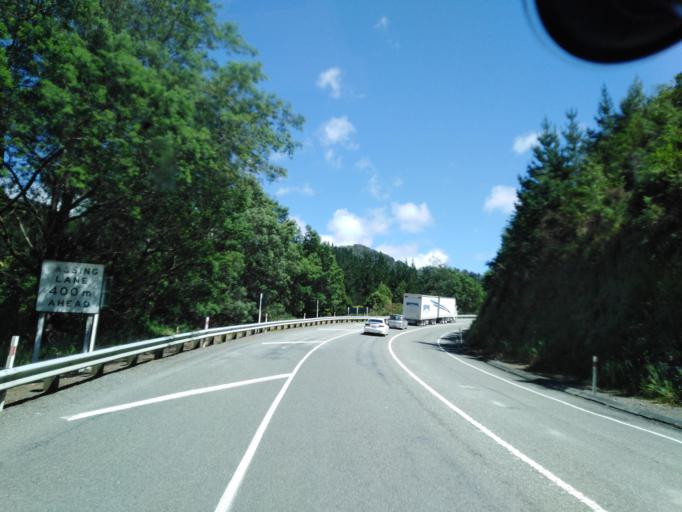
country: NZ
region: Nelson
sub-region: Nelson City
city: Nelson
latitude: -41.1974
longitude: 173.5592
